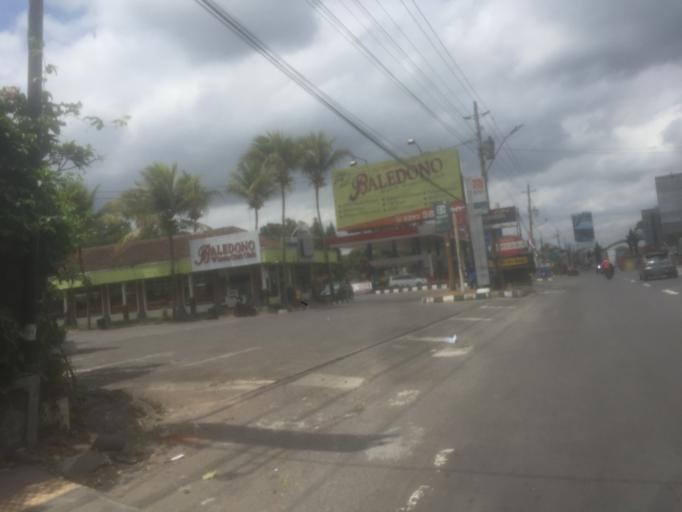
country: ID
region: Central Java
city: Muntilan
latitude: -7.6396
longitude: 110.3220
